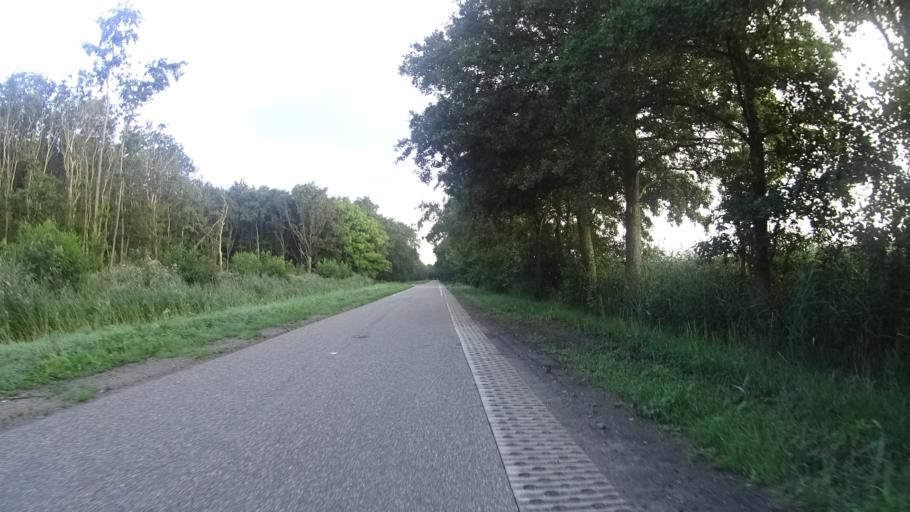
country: NL
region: North Holland
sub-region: Gemeente Hollands Kroon
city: Den Oever
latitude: 52.9186
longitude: 5.0515
